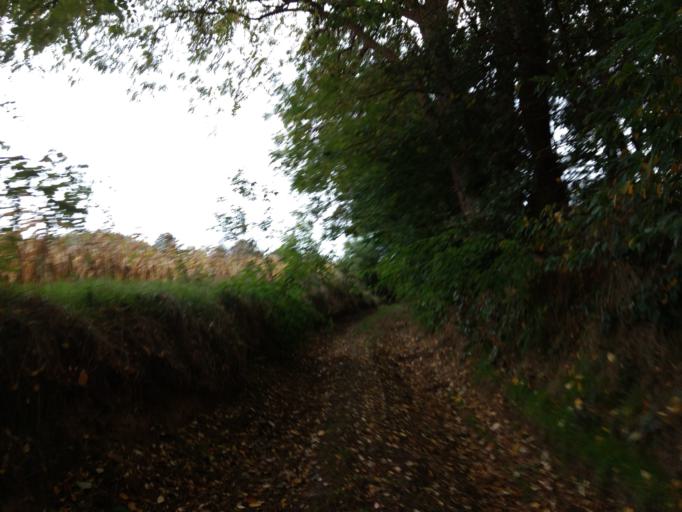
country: BE
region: Flanders
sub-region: Provincie Vlaams-Brabant
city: Diest
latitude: 50.9646
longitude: 5.0234
